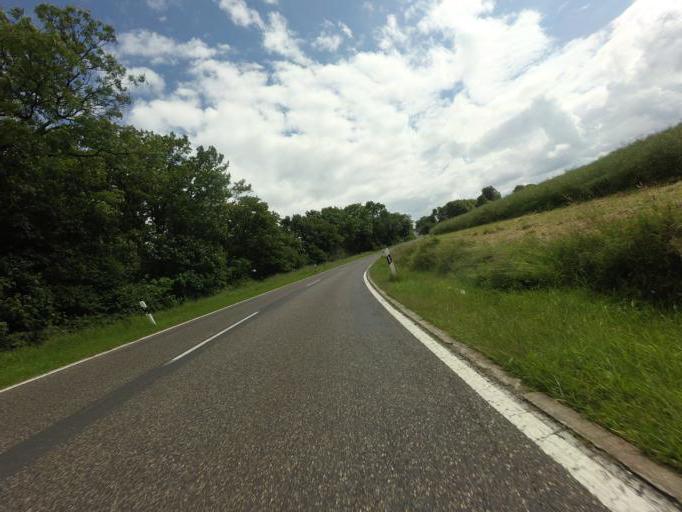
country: DE
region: Rheinland-Pfalz
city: Dungenheim
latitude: 50.2763
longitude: 7.1559
